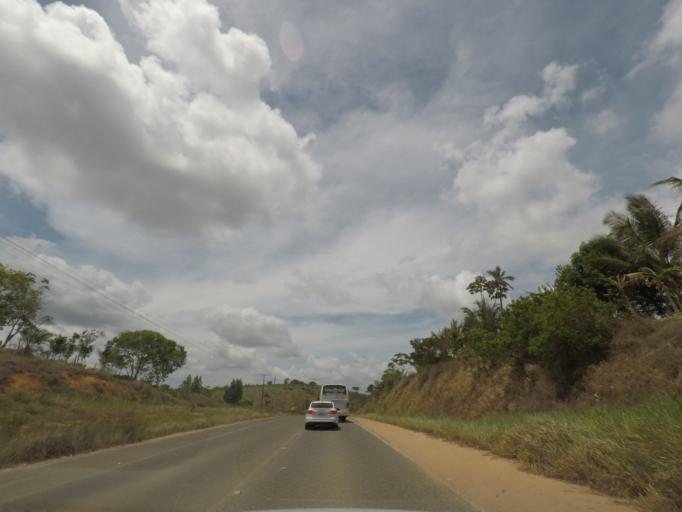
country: BR
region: Sergipe
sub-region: Indiaroba
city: Indiaroba
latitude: -11.5362
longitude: -37.5615
